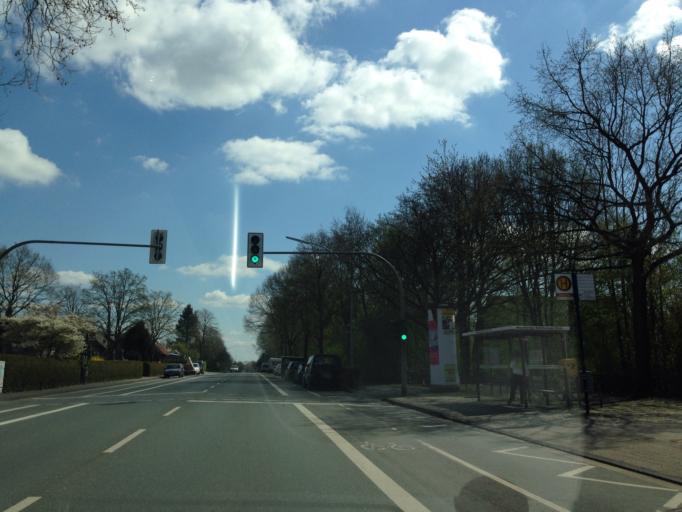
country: DE
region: North Rhine-Westphalia
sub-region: Regierungsbezirk Munster
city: Muenster
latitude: 51.9979
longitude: 7.5623
